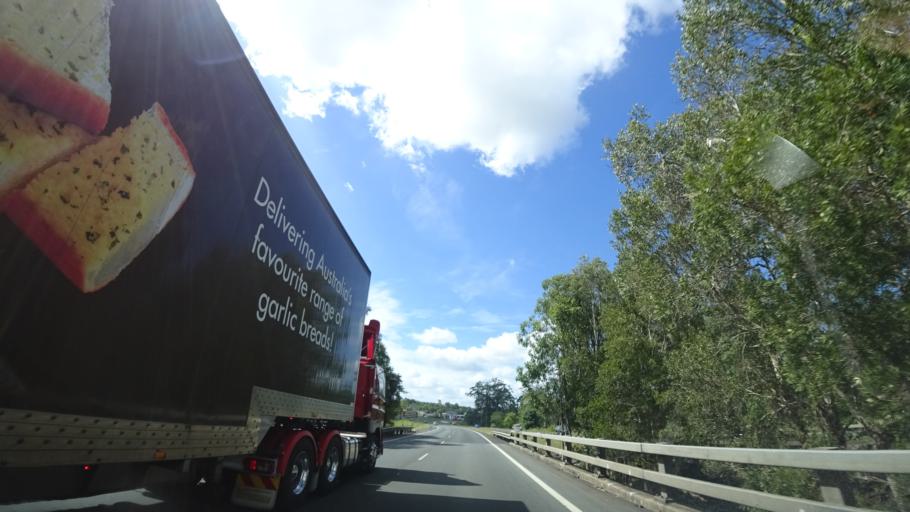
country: AU
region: Queensland
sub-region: Sunshine Coast
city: Woombye
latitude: -26.6822
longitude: 153.0029
